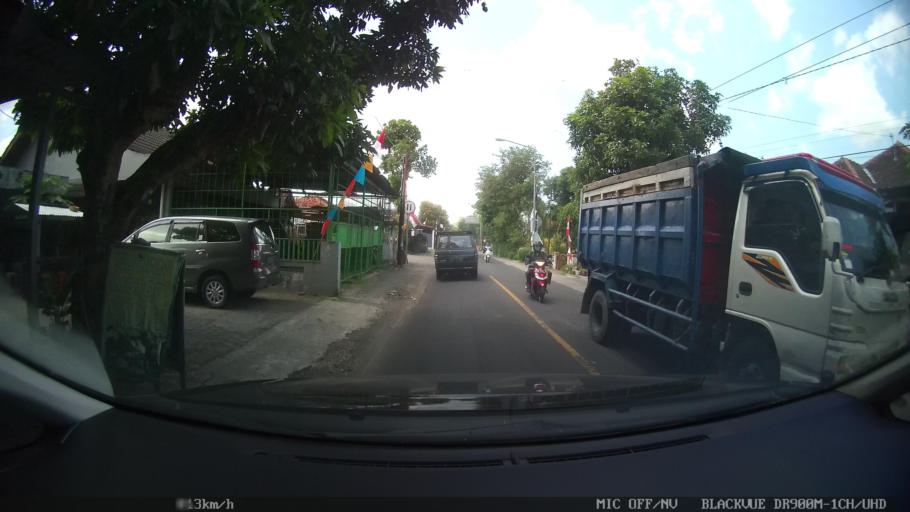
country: ID
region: Daerah Istimewa Yogyakarta
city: Bantul
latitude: -7.9078
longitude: 110.3447
